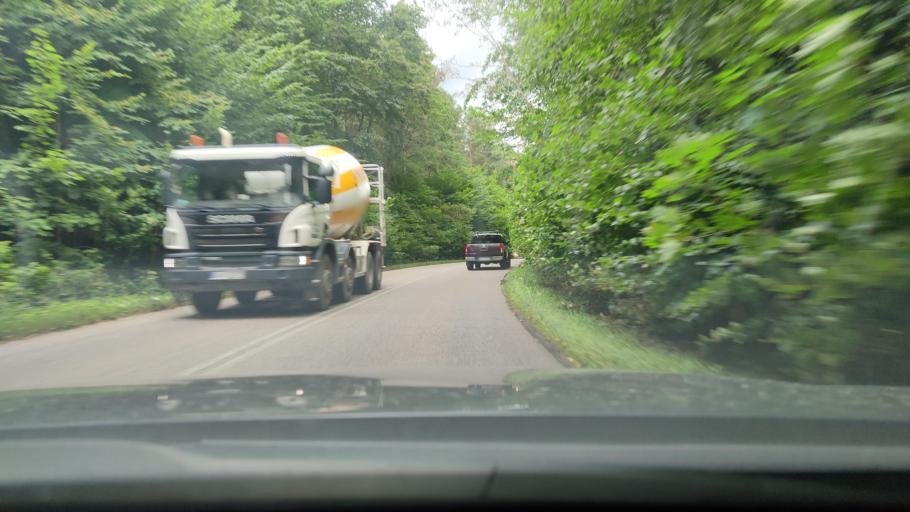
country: PL
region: Pomeranian Voivodeship
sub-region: Powiat pucki
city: Krokowa
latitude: 54.7297
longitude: 18.1696
